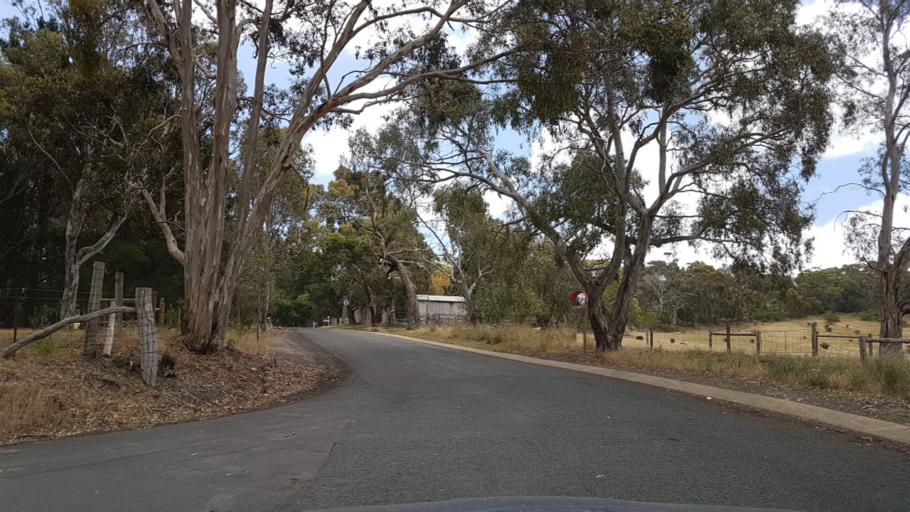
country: AU
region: South Australia
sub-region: Victor Harbor
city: Victor Harbor
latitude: -35.4628
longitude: 138.5930
